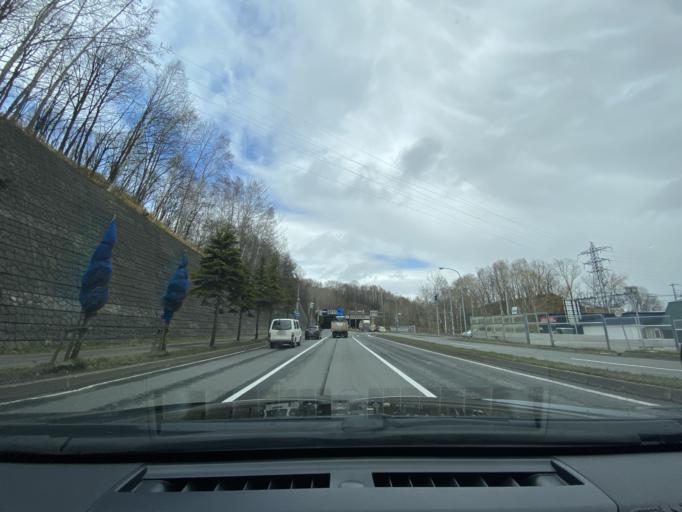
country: JP
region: Hokkaido
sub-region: Asahikawa-shi
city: Asahikawa
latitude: 43.8009
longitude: 142.3421
